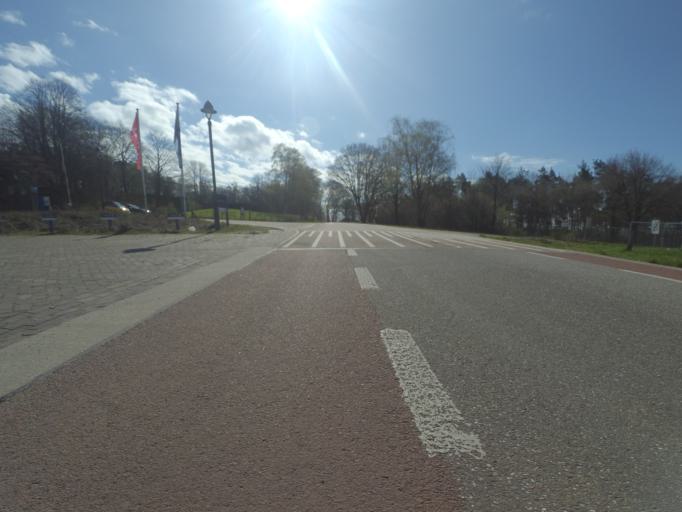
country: NL
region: Gelderland
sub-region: Gemeente Arnhem
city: Hoogkamp
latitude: 52.0629
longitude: 5.8960
